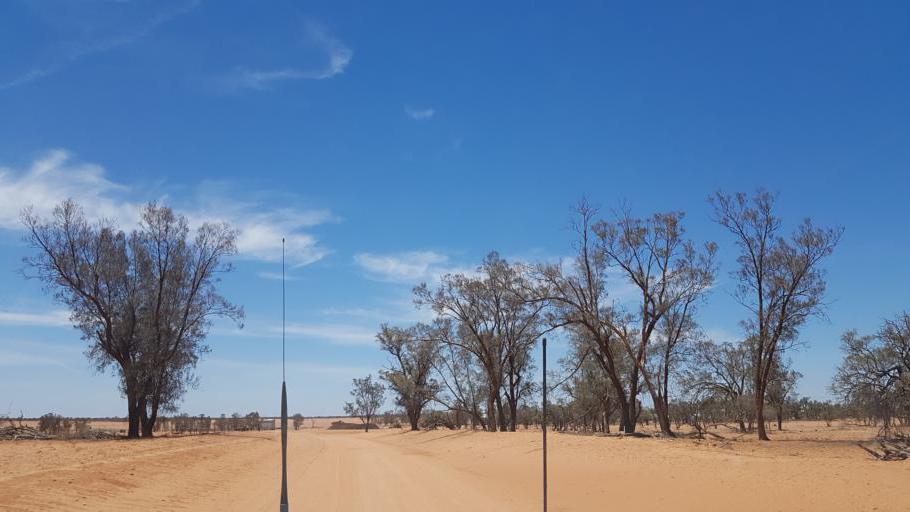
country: AU
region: New South Wales
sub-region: Wentworth
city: Dareton
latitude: -33.3450
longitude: 141.4517
